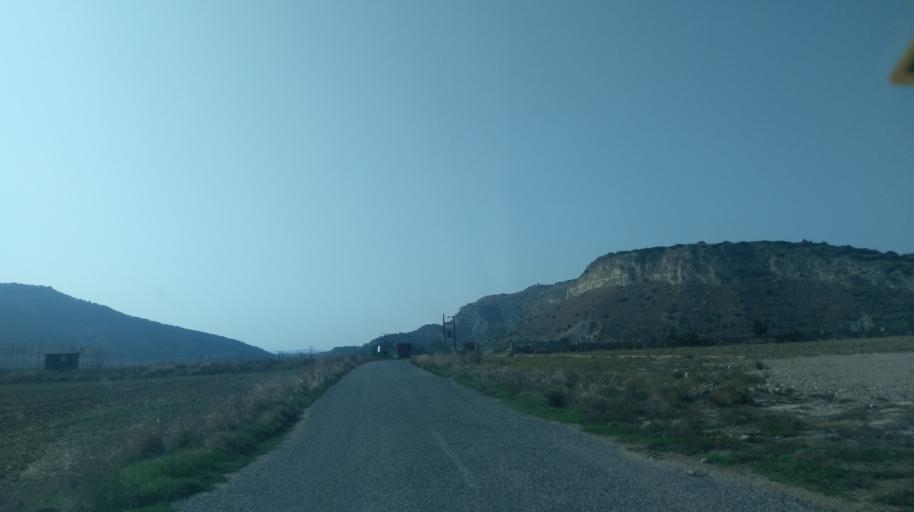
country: CY
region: Ammochostos
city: Rizokarpaso
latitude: 35.5158
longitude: 34.3053
